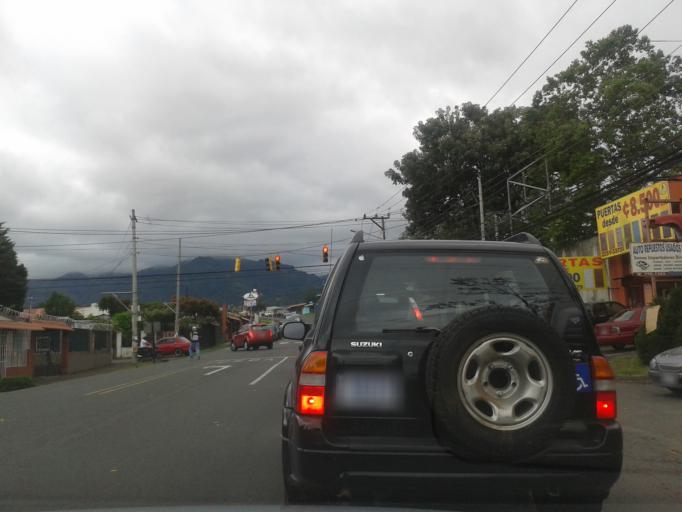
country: CR
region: San Jose
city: San Rafael Arriba
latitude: 9.8813
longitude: -84.0715
